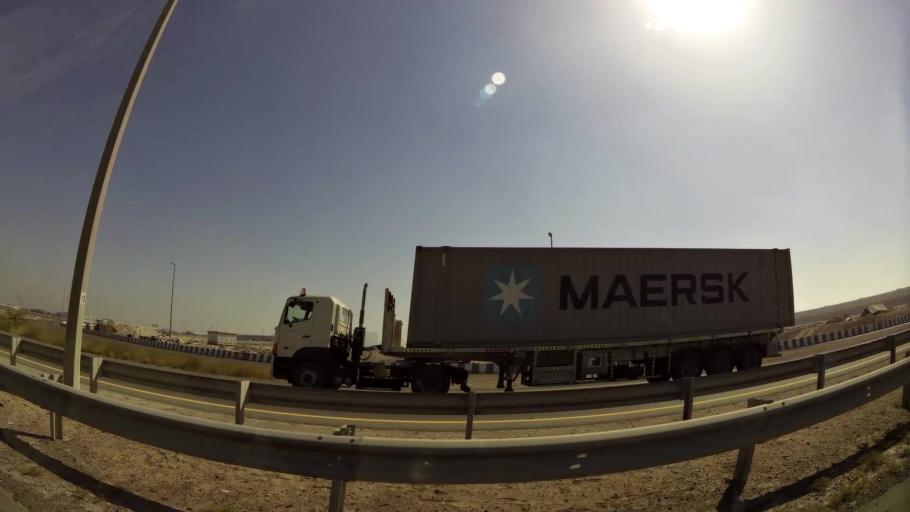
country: AE
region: Dubai
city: Dubai
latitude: 24.9426
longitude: 55.0673
